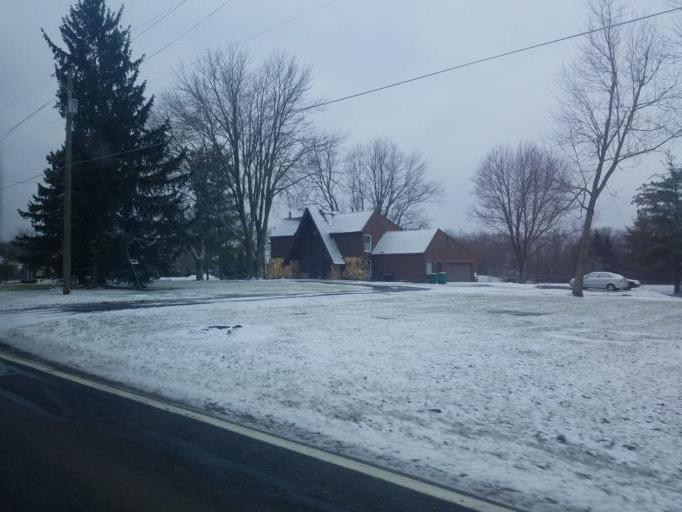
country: US
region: Ohio
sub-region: Franklin County
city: New Albany
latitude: 40.0345
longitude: -82.7885
